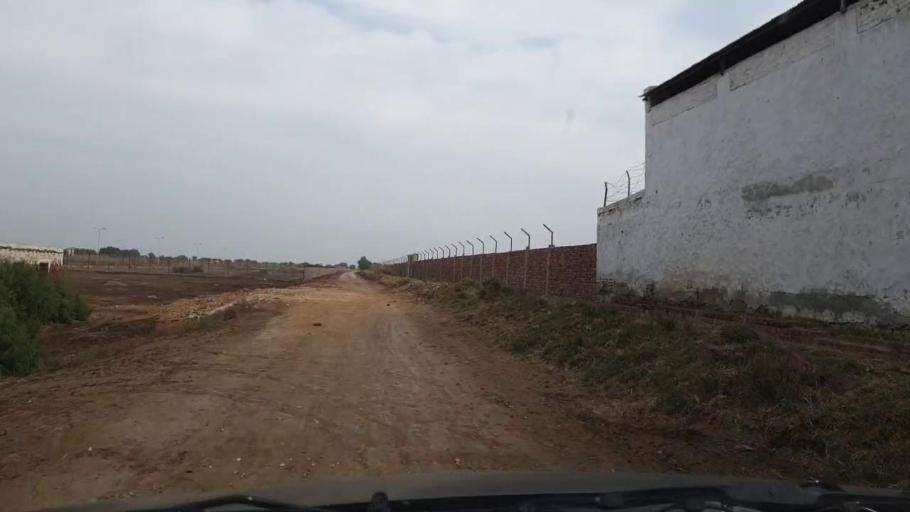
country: PK
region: Sindh
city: Sanghar
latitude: 26.0914
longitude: 68.8786
